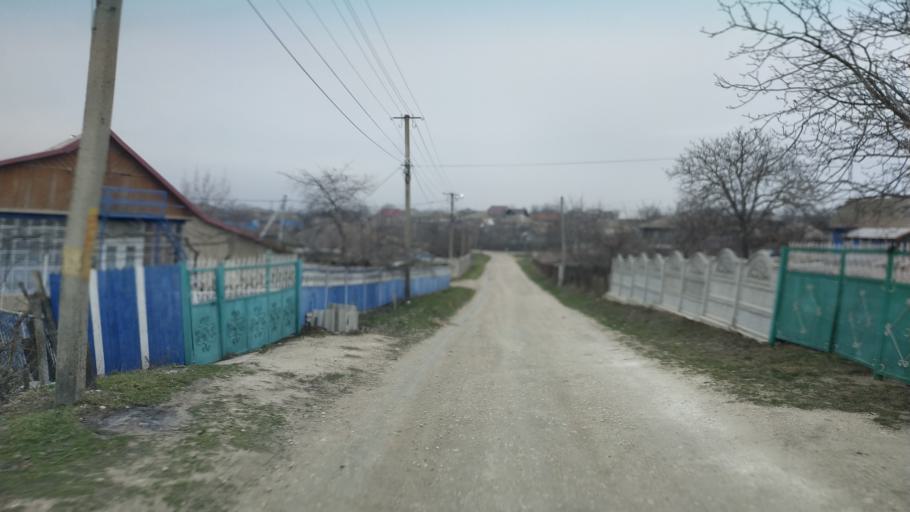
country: MD
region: Chisinau
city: Singera
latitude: 46.8248
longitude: 29.0269
